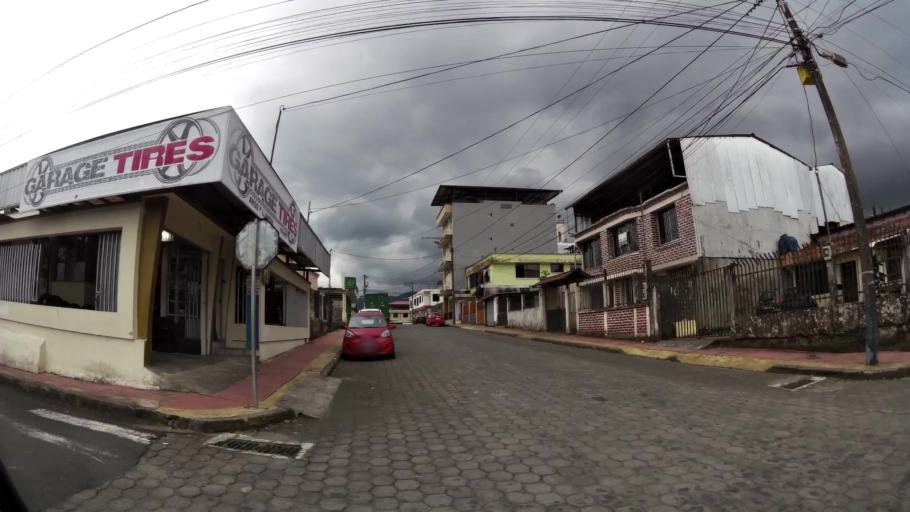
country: EC
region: Pastaza
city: Puyo
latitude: -1.4895
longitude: -77.9997
